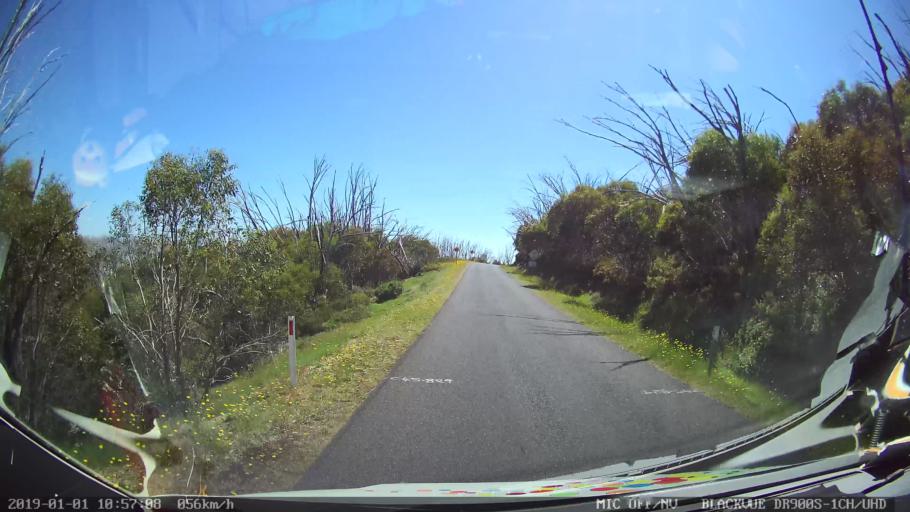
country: AU
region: New South Wales
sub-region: Snowy River
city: Jindabyne
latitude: -35.9994
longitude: 148.3950
